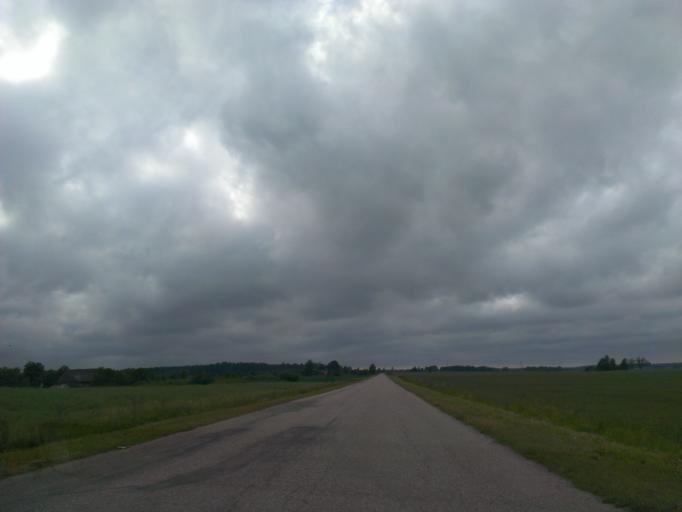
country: LV
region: Aizpute
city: Aizpute
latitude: 56.7146
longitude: 21.4678
